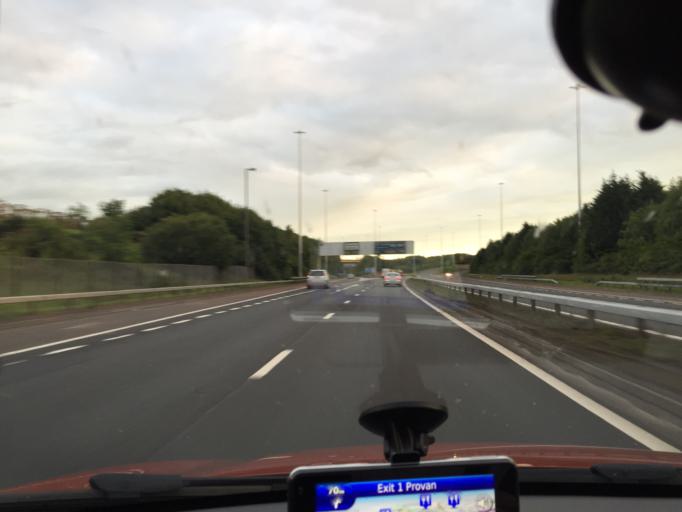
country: GB
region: Scotland
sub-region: East Dunbartonshire
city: Bishopbriggs
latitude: 55.8764
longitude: -4.1982
